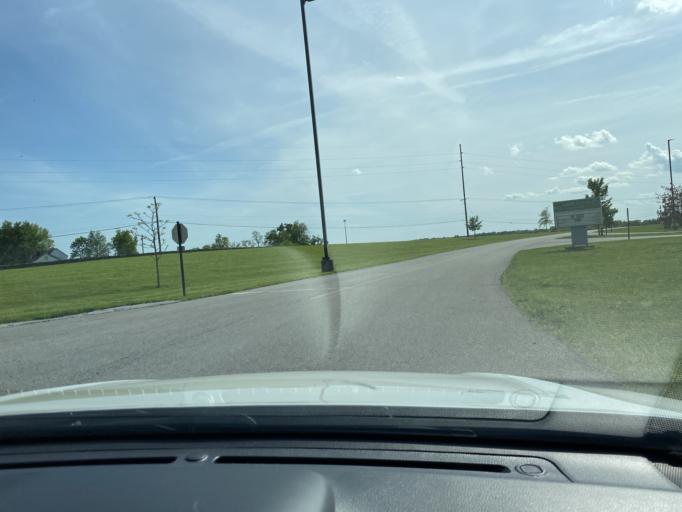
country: US
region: Kentucky
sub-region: Scott County
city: Georgetown
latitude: 38.2111
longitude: -84.5997
